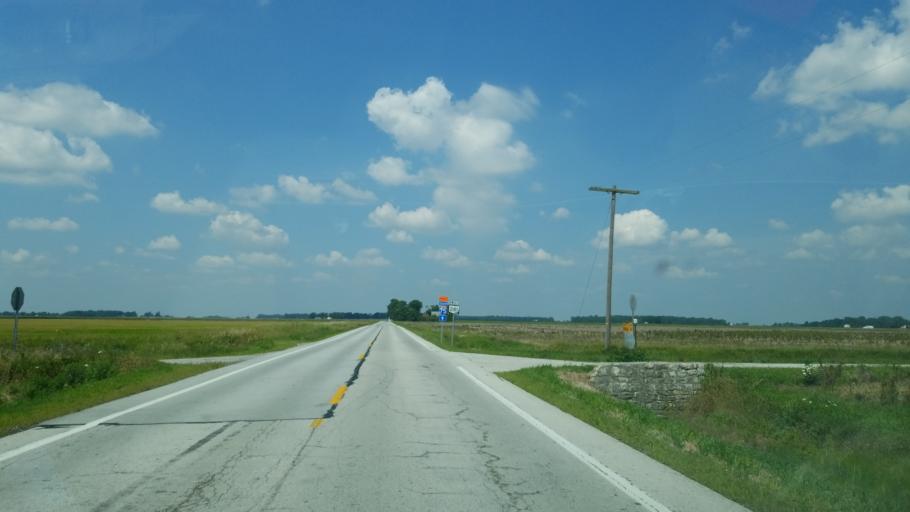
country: US
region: Ohio
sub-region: Wood County
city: Bowling Green
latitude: 41.2834
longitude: -83.6888
